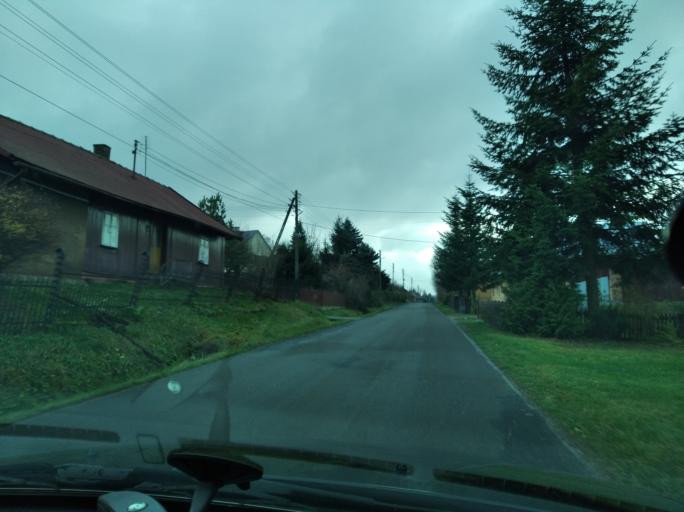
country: PL
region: Subcarpathian Voivodeship
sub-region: Powiat przeworski
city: Sietesz
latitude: 49.9926
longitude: 22.3539
